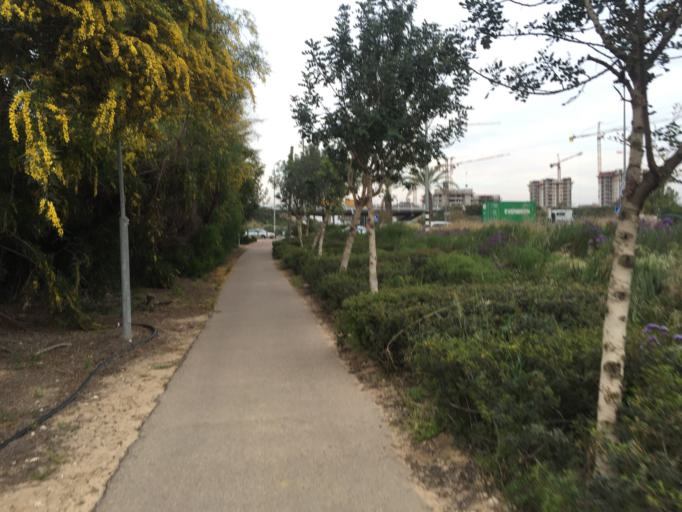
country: IL
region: Haifa
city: Qesarya
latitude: 32.5048
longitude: 34.9125
